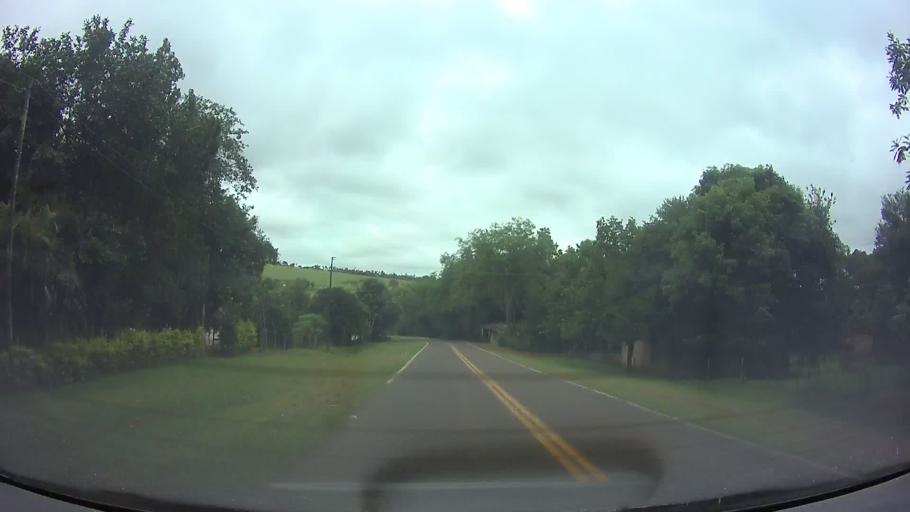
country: PY
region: Paraguari
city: Acahay
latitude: -25.9307
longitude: -57.1059
